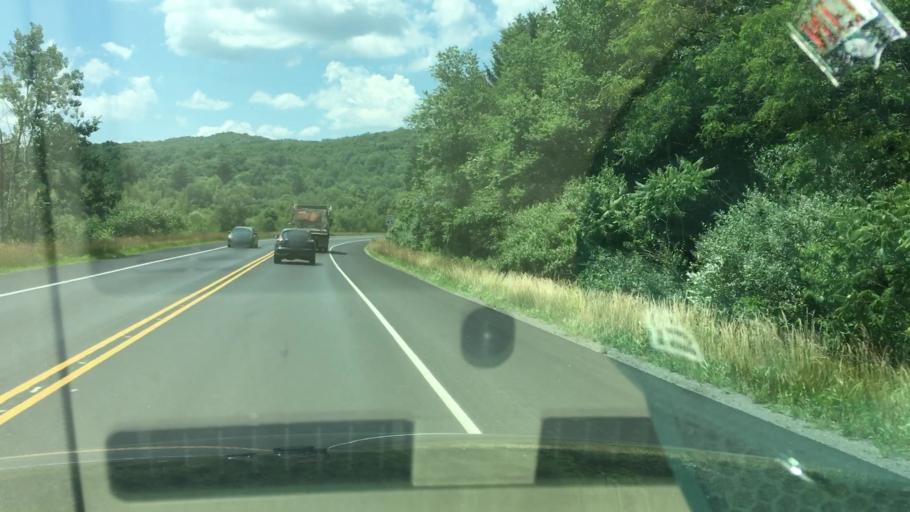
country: US
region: Pennsylvania
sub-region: Northumberland County
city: Mount Carmel
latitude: 40.7694
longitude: -76.4376
